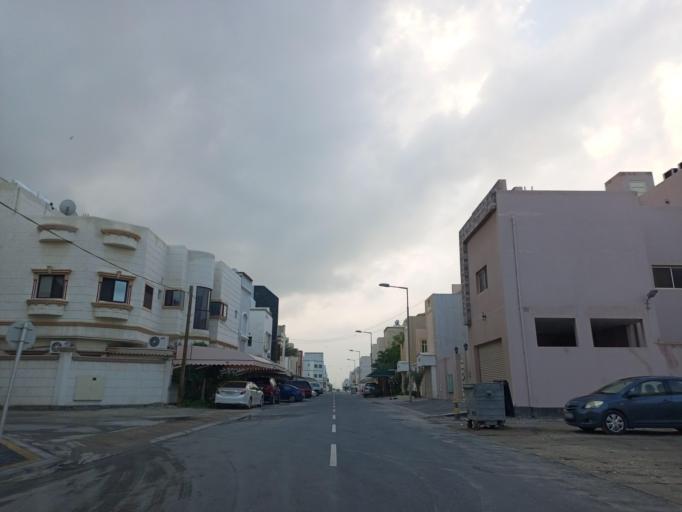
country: BH
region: Muharraq
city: Al Hadd
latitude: 26.2353
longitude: 50.6499
